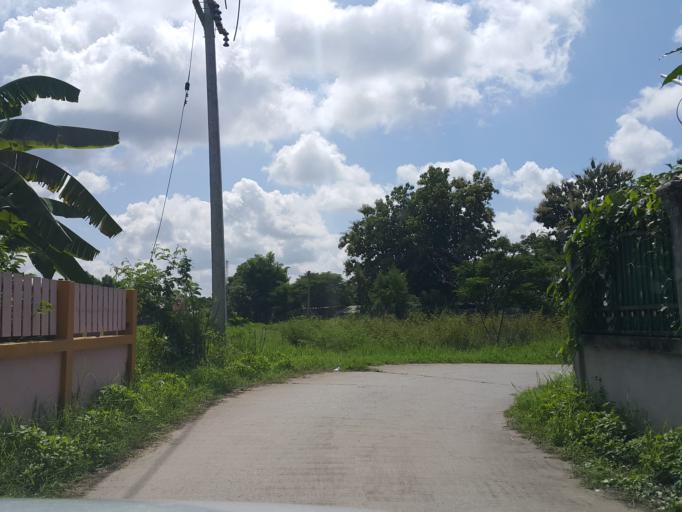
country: TH
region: Chiang Mai
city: San Kamphaeng
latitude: 18.7458
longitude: 99.1130
